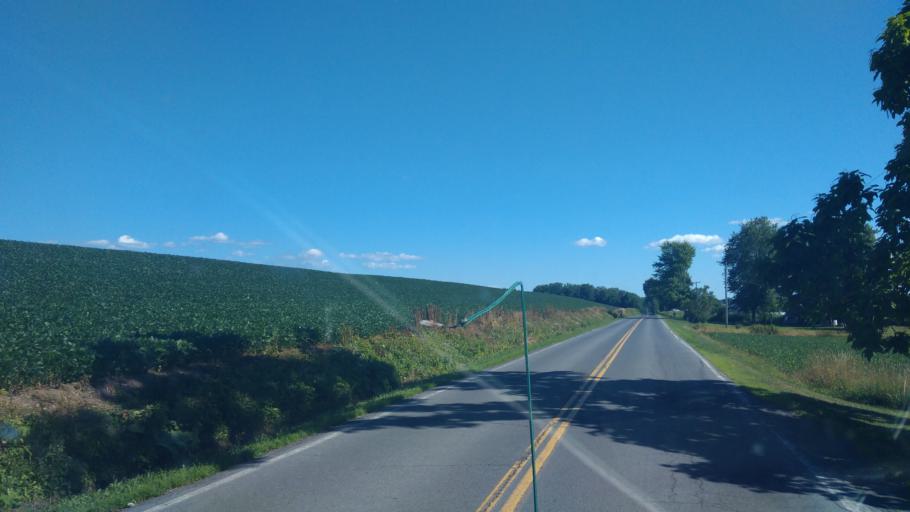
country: US
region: New York
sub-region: Wayne County
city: Clyde
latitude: 43.0187
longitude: -76.8126
